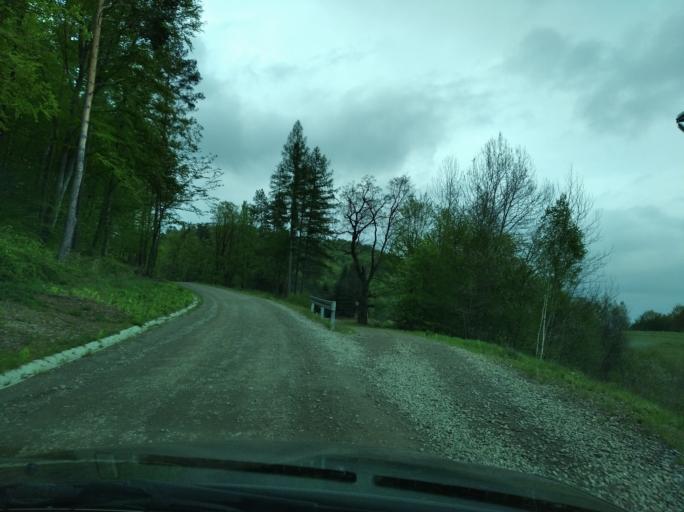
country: PL
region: Subcarpathian Voivodeship
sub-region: Powiat sanocki
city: Sanok
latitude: 49.5650
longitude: 22.2326
